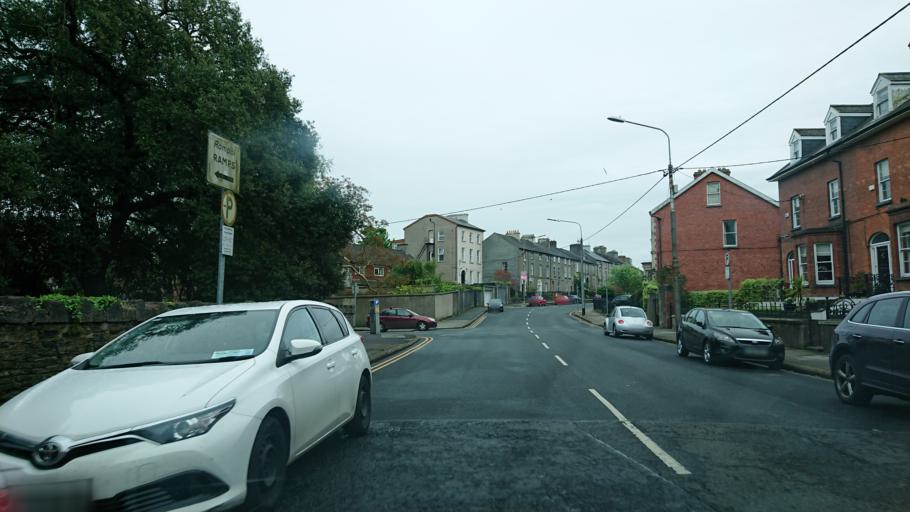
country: IE
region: Munster
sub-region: Waterford
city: Waterford
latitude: 52.2559
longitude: -7.1072
